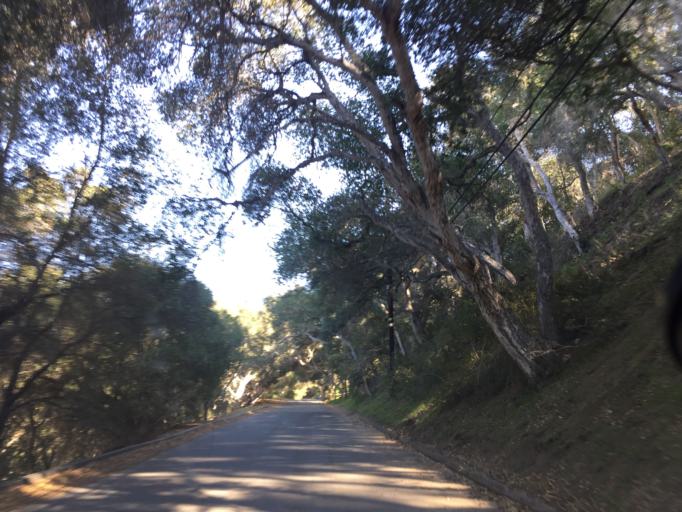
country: US
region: California
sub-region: Santa Barbara County
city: Goleta
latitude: 34.4322
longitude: -119.7789
